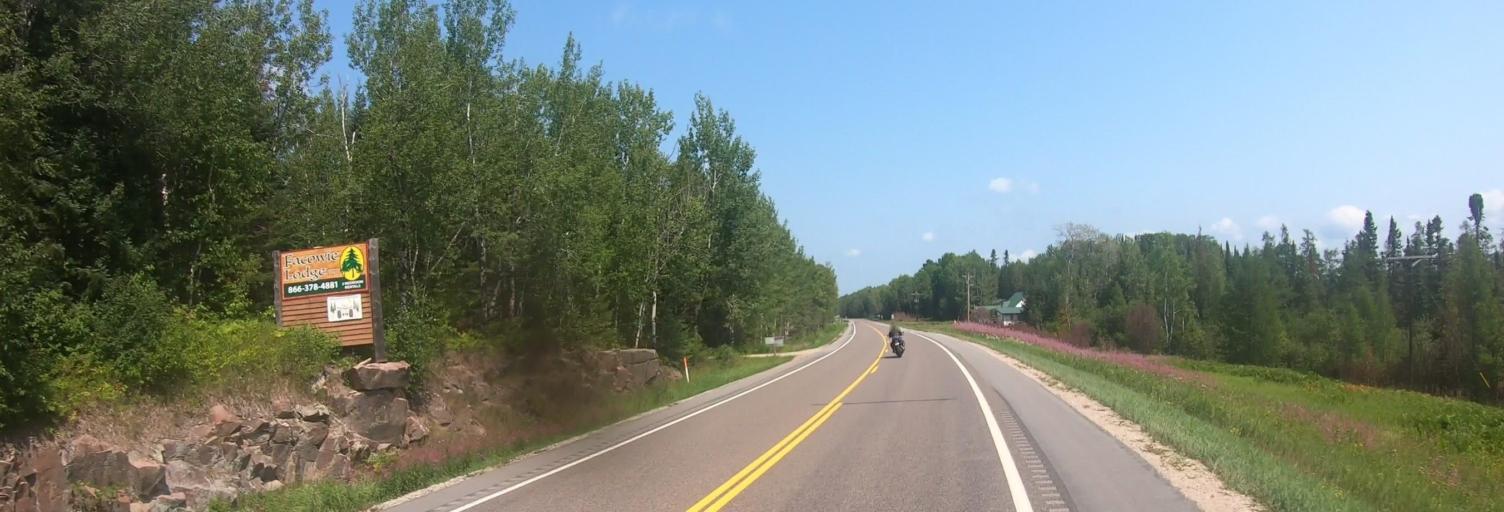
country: US
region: Minnesota
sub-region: Saint Louis County
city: Parkville
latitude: 48.1750
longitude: -92.5123
